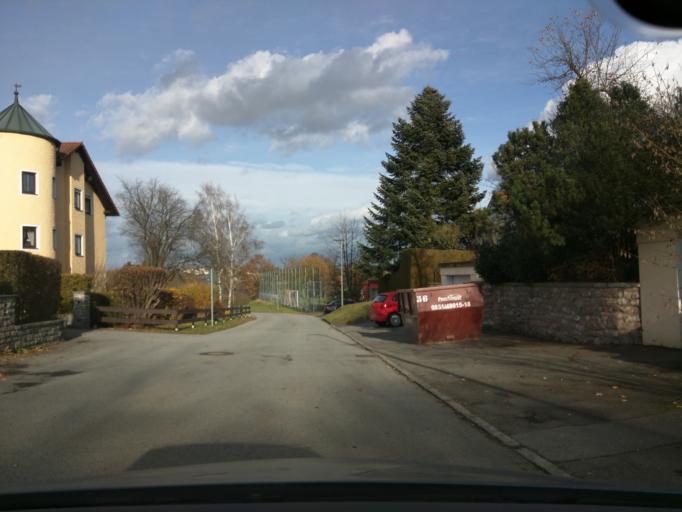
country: DE
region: Bavaria
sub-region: Lower Bavaria
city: Passau
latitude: 48.5652
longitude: 13.4202
